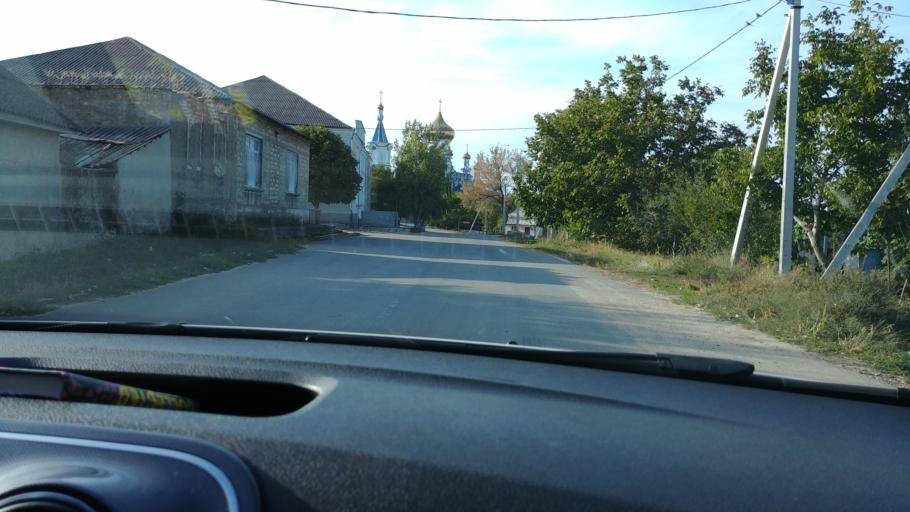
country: MD
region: Rezina
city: Rezina
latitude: 47.7496
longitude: 28.8818
